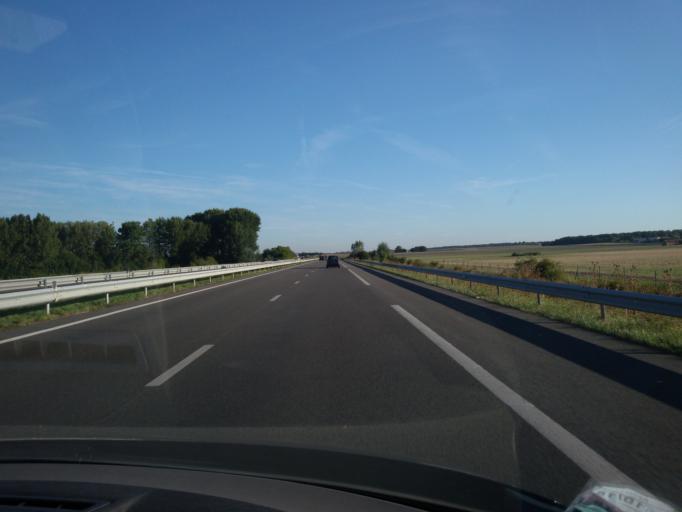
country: FR
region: Centre
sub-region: Departement du Cher
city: Chateauneuf-sur-Cher
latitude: 46.8139
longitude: 2.4127
